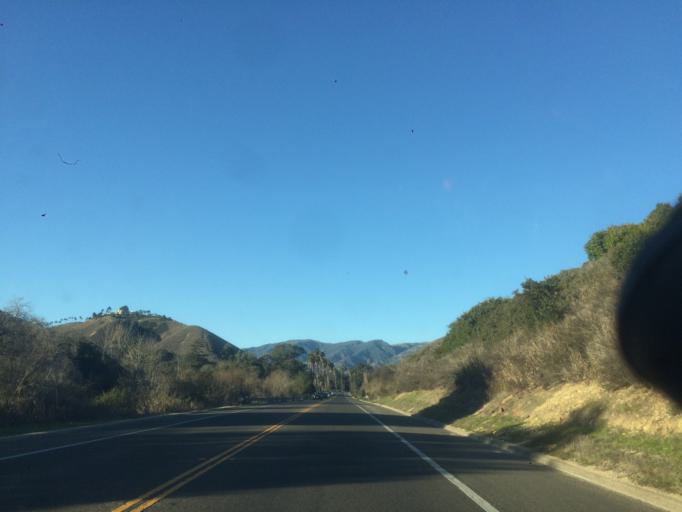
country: US
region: California
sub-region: Santa Barbara County
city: Santa Barbara
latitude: 34.4067
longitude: -119.7396
